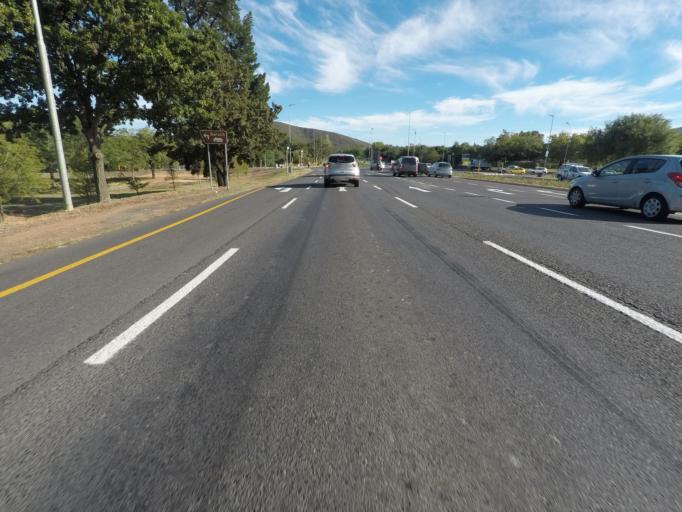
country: ZA
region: Western Cape
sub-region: Cape Winelands District Municipality
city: Stellenbosch
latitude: -33.9491
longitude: 18.8543
